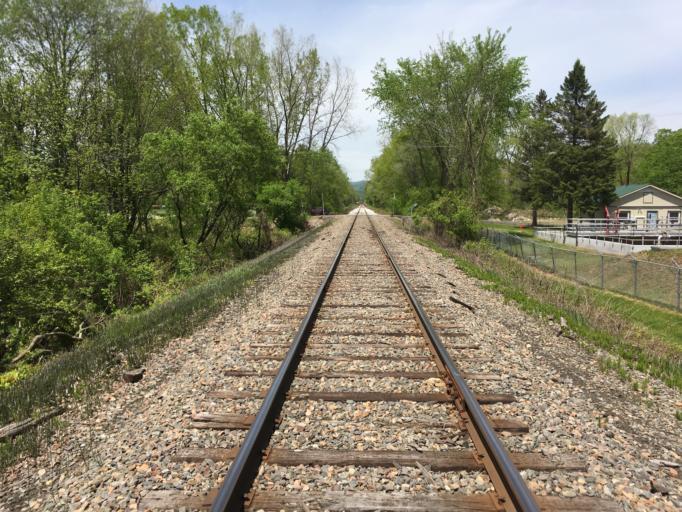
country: US
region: Vermont
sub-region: Windsor County
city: Chester
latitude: 43.2555
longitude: -72.5763
